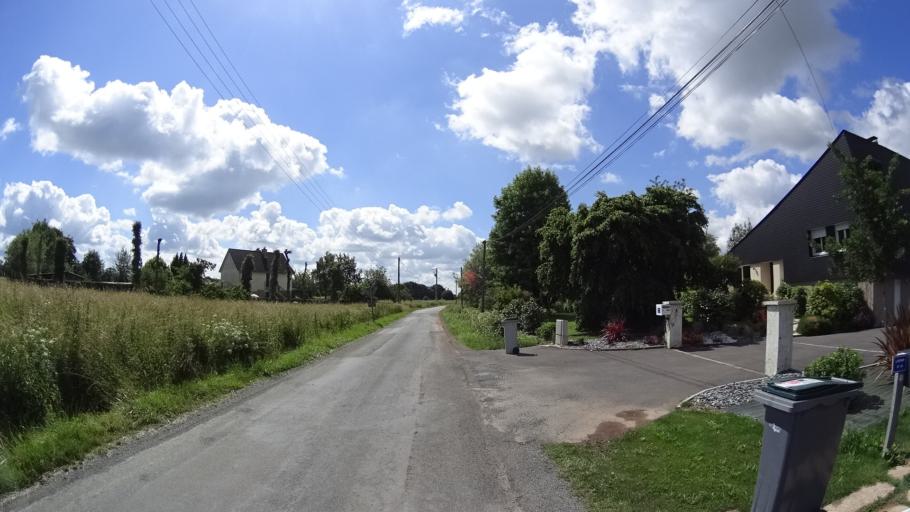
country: FR
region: Brittany
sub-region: Departement d'Ille-et-Vilaine
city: Le Rheu
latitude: 48.1157
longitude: -1.8162
